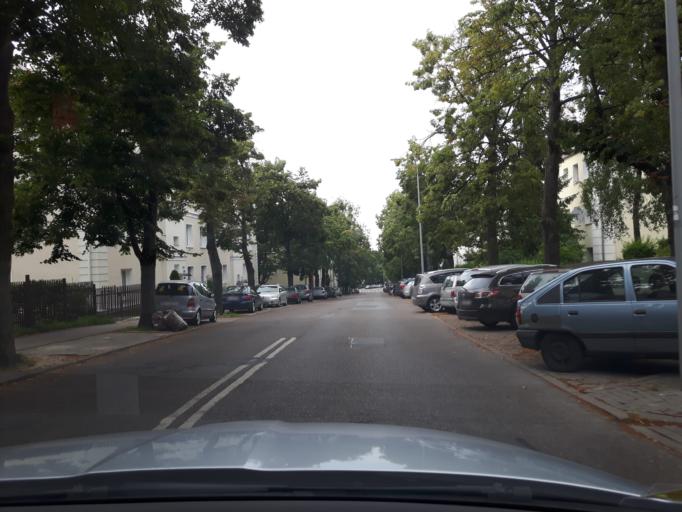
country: PL
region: Pomeranian Voivodeship
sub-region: Gdynia
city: Gdynia
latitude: 54.5045
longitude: 18.5396
